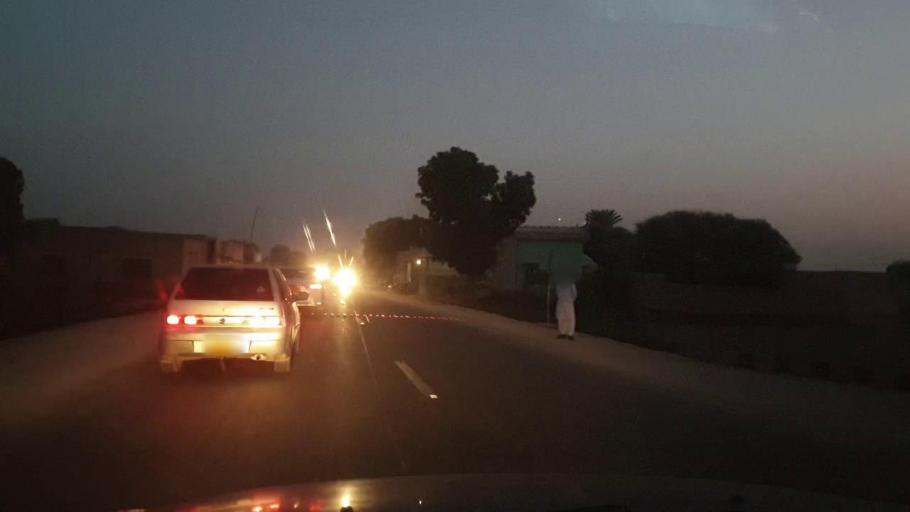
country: PK
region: Sindh
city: Chambar
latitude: 25.3765
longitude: 68.7788
